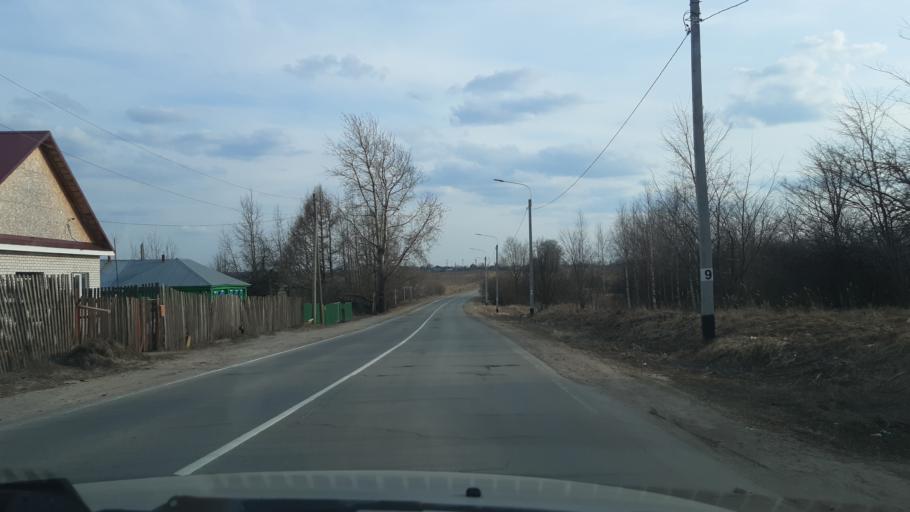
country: RU
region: Vladimir
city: Nikologory
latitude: 56.1602
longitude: 41.9955
